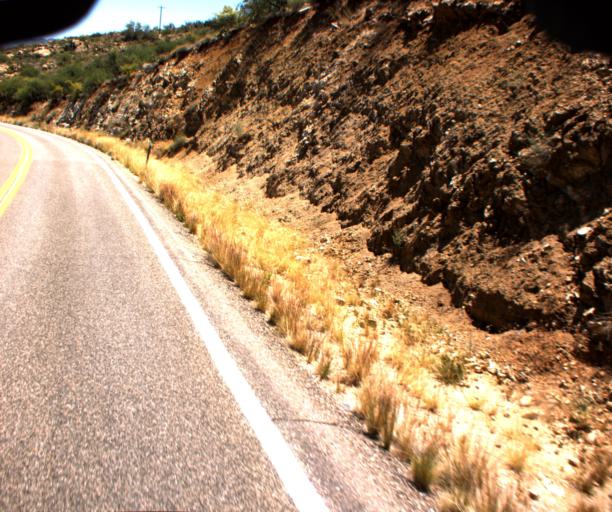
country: US
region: Arizona
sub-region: Yavapai County
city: Bagdad
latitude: 34.5194
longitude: -113.0969
